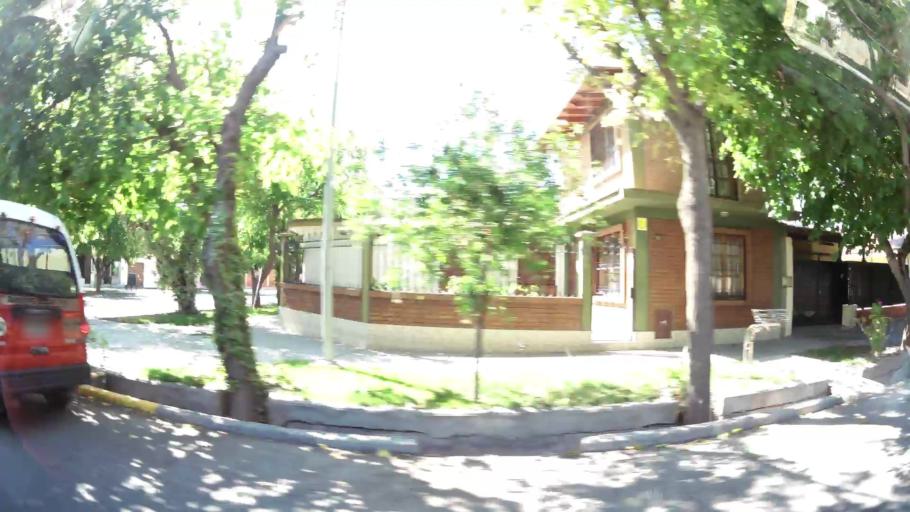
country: AR
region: Mendoza
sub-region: Departamento de Godoy Cruz
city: Godoy Cruz
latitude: -32.9628
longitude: -68.8432
